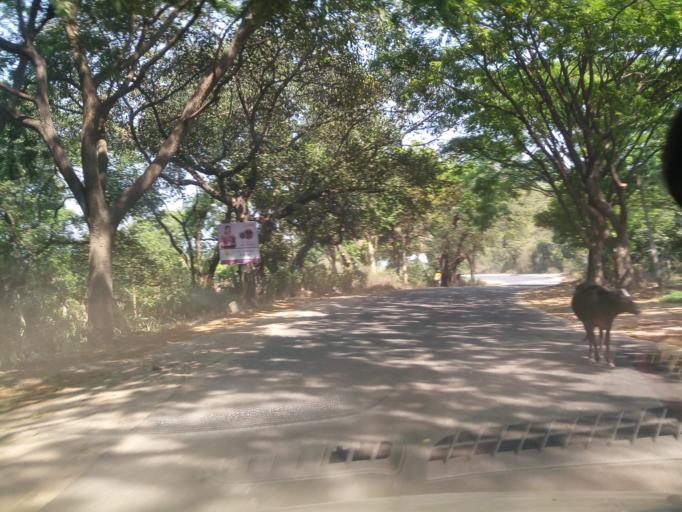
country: IN
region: Karnataka
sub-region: Hassan
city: Sakleshpur
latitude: 12.9493
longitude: 75.8069
